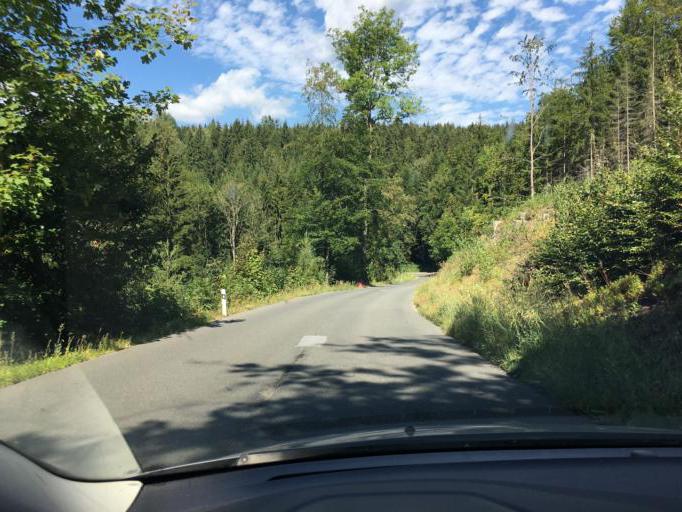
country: CZ
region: Liberecky
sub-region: Okres Semily
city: Vysoke nad Jizerou
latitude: 50.7075
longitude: 15.3744
